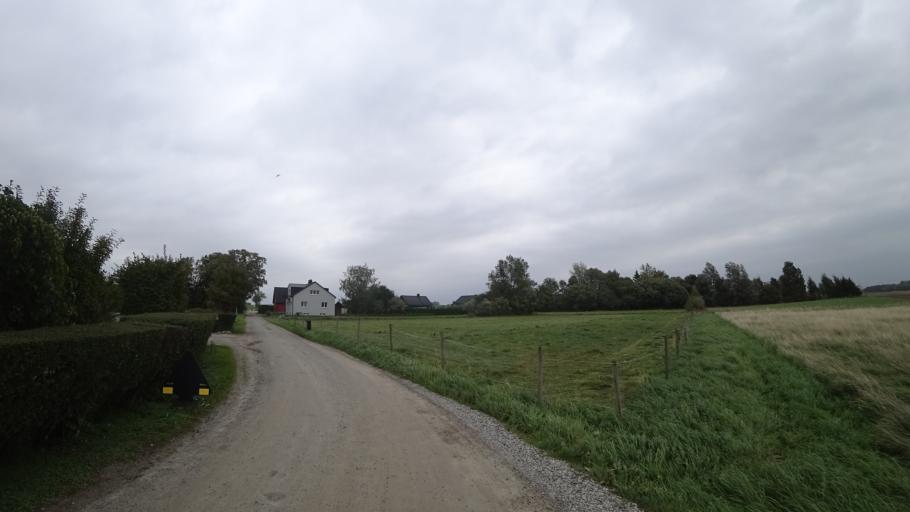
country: SE
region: Skane
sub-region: Kavlinge Kommun
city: Kaevlinge
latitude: 55.7991
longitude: 13.1405
